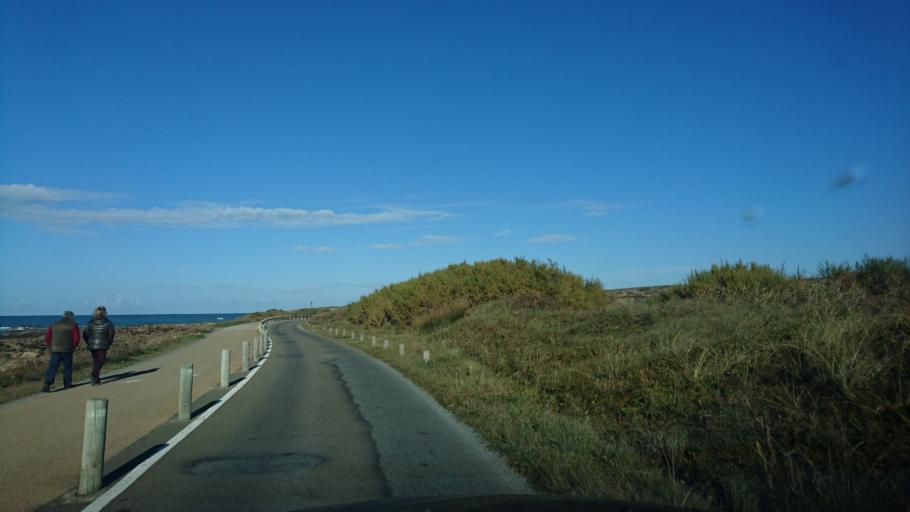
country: FR
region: Pays de la Loire
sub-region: Departement de la Vendee
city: Les Sables-d'Olonne
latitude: 46.5083
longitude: -1.8174
